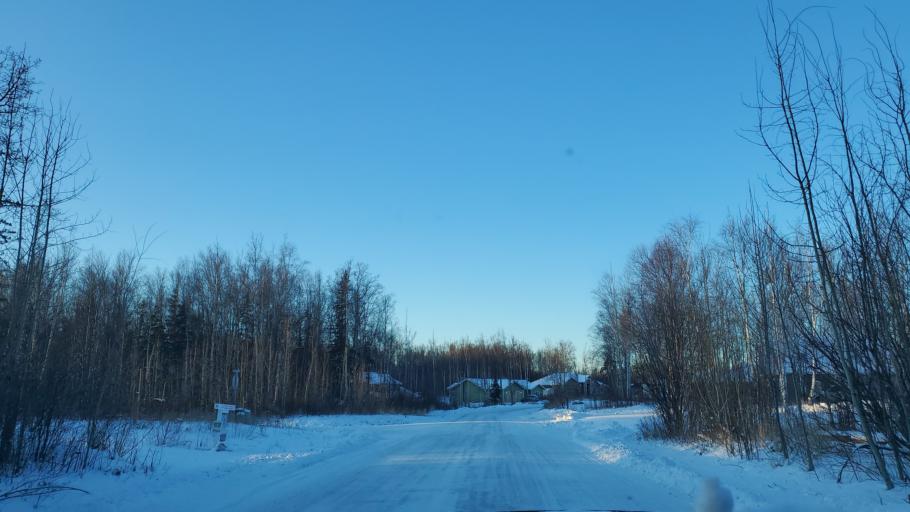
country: US
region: Alaska
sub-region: Matanuska-Susitna Borough
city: Lakes
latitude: 61.6392
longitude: -149.3092
